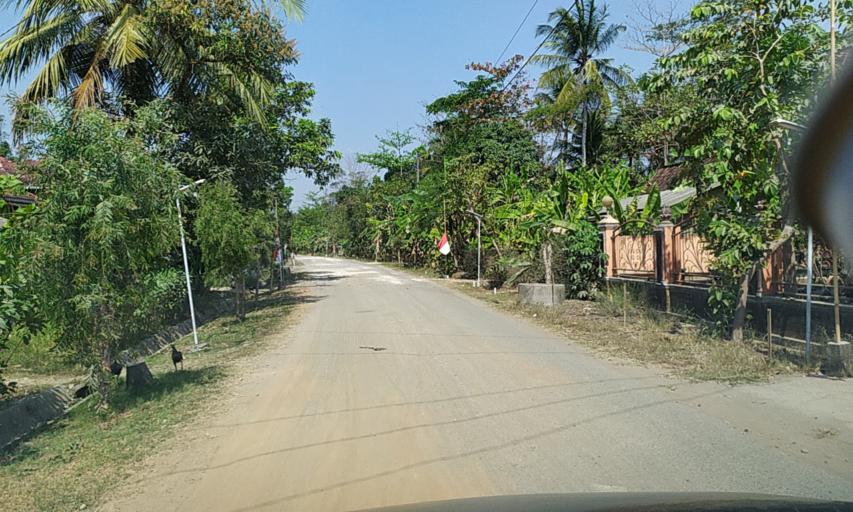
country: ID
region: Central Java
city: Mulyosari
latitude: -7.5023
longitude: 108.7904
